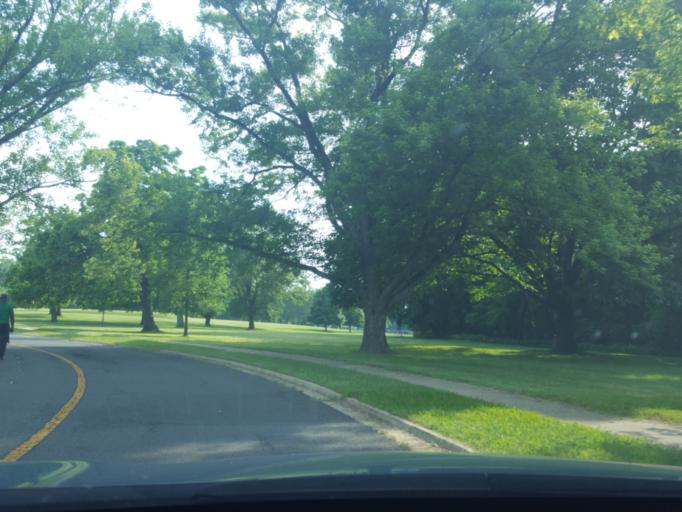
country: US
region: Maryland
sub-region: Prince George's County
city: Fort Washington
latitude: 38.7150
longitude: -77.0281
